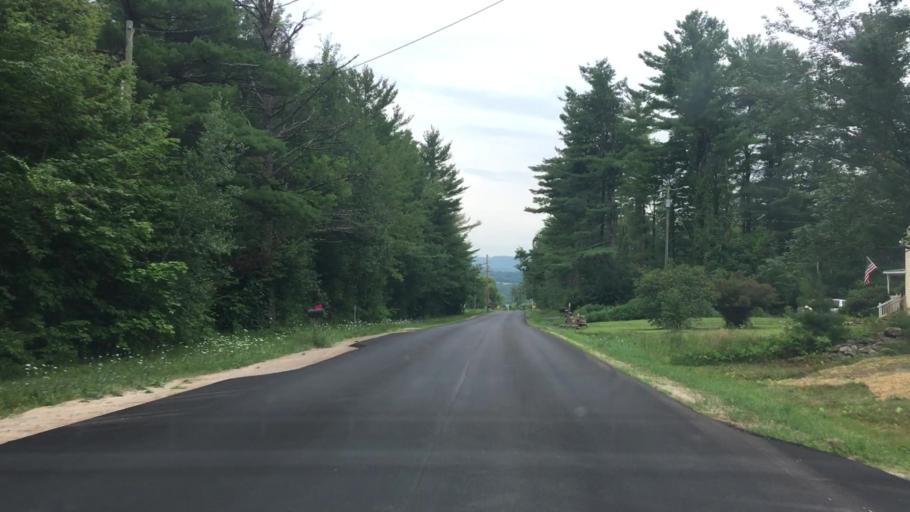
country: US
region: New York
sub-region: Clinton County
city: Peru
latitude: 44.5497
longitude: -73.5647
